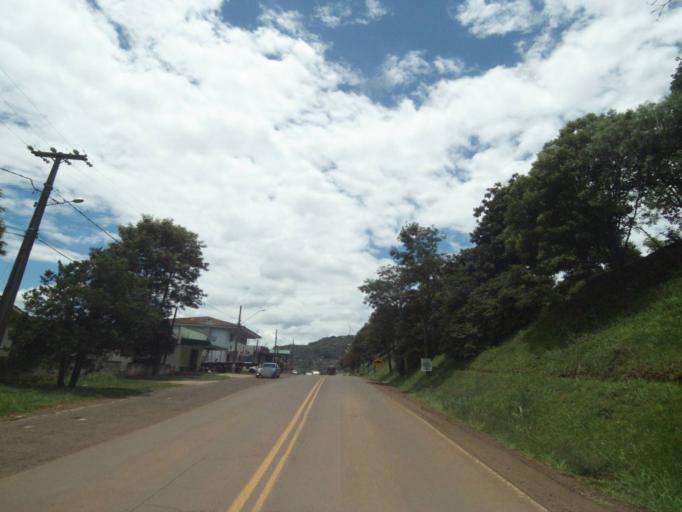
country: BR
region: Parana
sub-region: Pinhao
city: Pinhao
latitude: -26.1568
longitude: -51.5621
